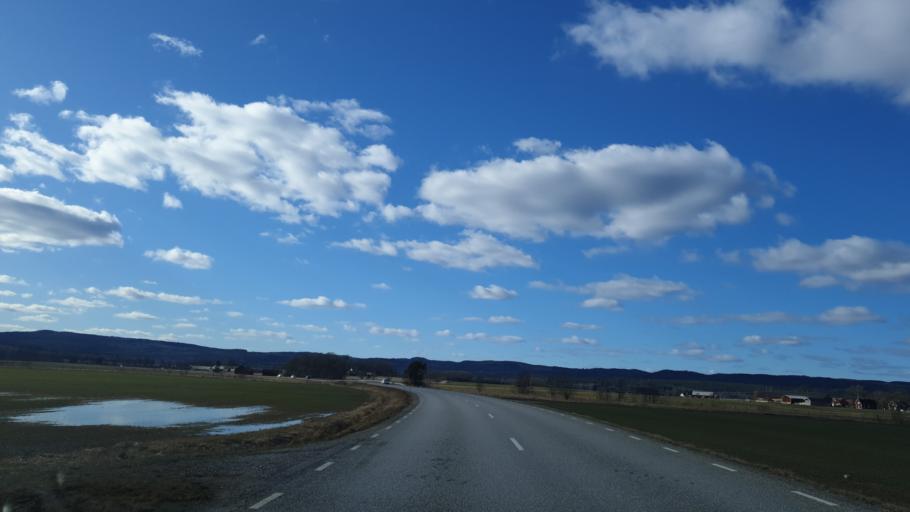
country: SE
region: OErebro
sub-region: Orebro Kommun
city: Garphyttan
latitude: 59.3403
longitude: 15.0570
